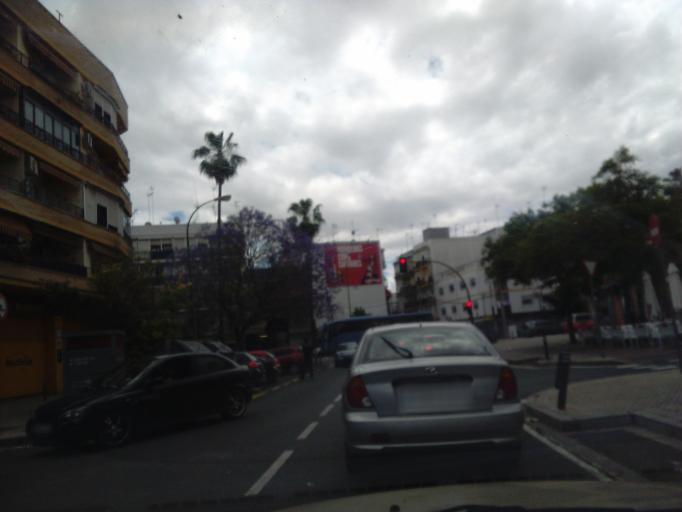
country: ES
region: Andalusia
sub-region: Provincia de Sevilla
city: Sevilla
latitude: 37.3714
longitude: -5.9517
